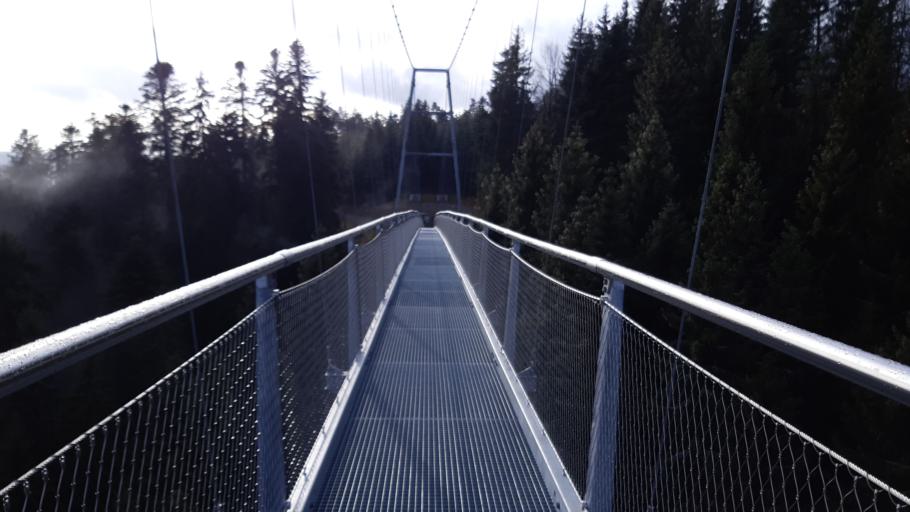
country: DE
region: Baden-Wuerttemberg
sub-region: Karlsruhe Region
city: Bad Wildbad
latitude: 48.7426
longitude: 8.5333
